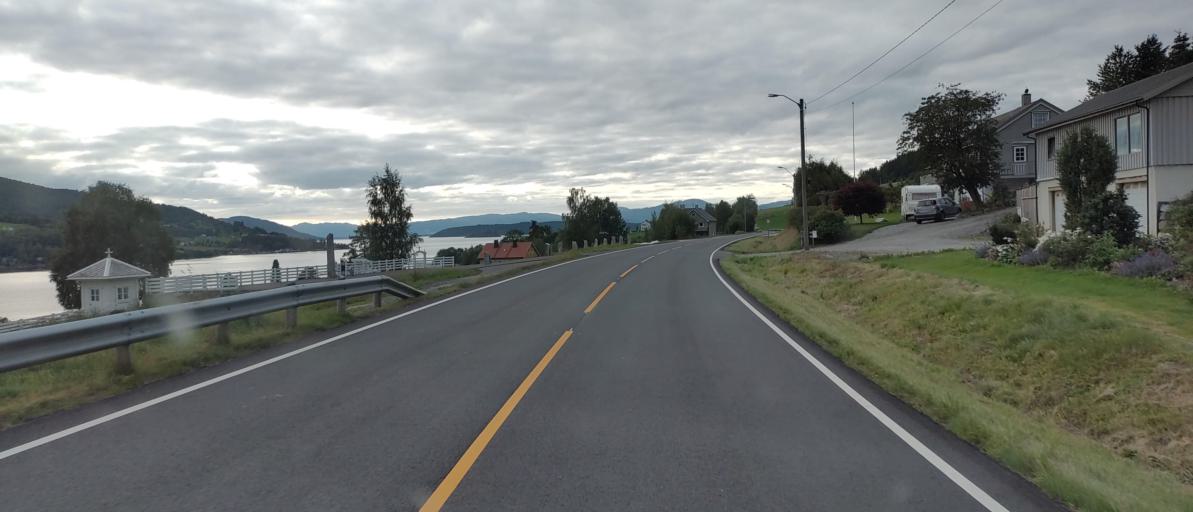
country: NO
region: More og Romsdal
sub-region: Molde
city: Hjelset
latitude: 62.6309
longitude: 7.5212
